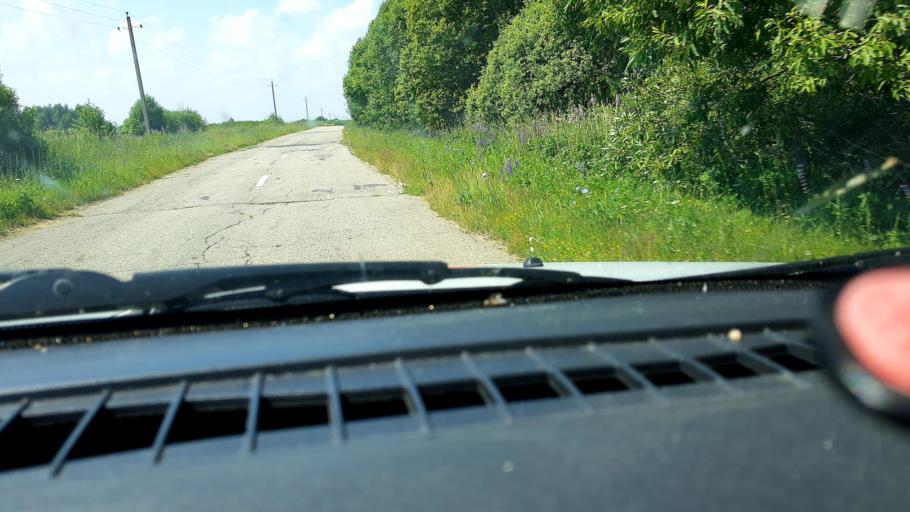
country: RU
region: Nizjnij Novgorod
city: Sharanga
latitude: 57.0613
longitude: 46.6258
